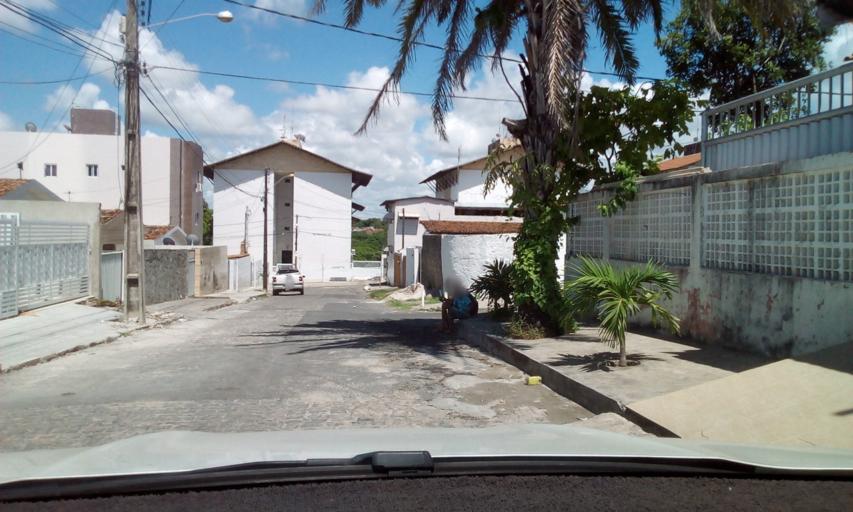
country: BR
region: Paraiba
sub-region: Joao Pessoa
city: Joao Pessoa
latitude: -7.1854
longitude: -34.8480
